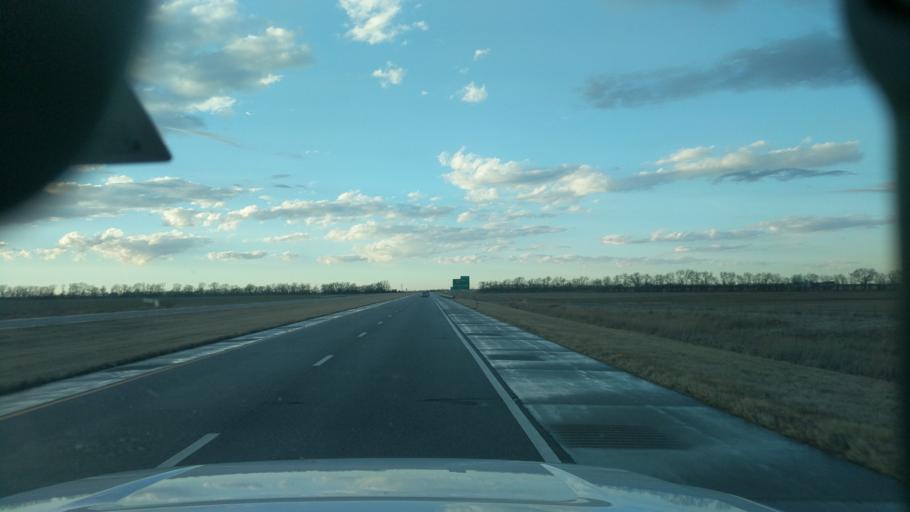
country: US
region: Kansas
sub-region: McPherson County
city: Moundridge
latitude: 38.1916
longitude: -97.4734
